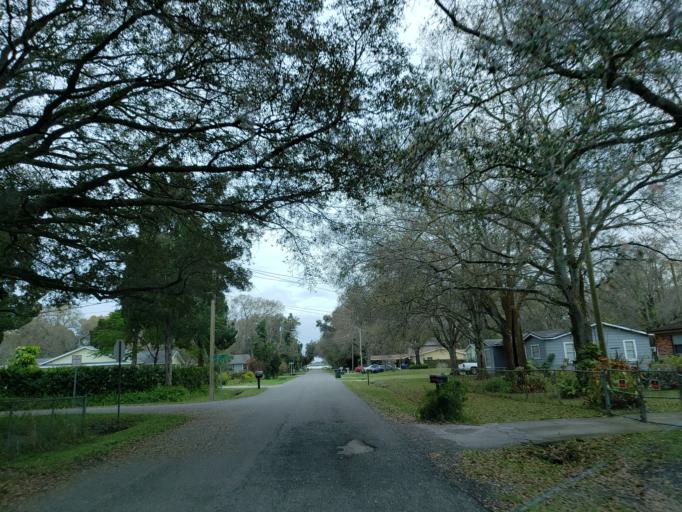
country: US
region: Florida
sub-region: Hillsborough County
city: Palm River-Clair Mel
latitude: 27.9187
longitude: -82.3729
